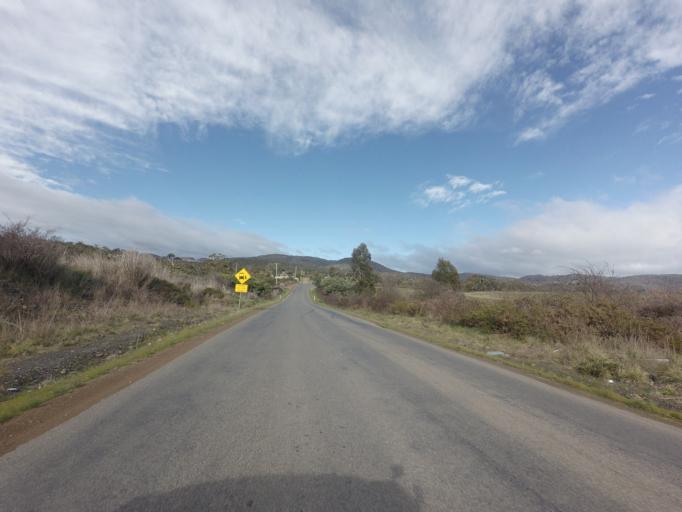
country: AU
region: Tasmania
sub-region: Derwent Valley
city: New Norfolk
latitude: -42.7763
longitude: 147.0202
